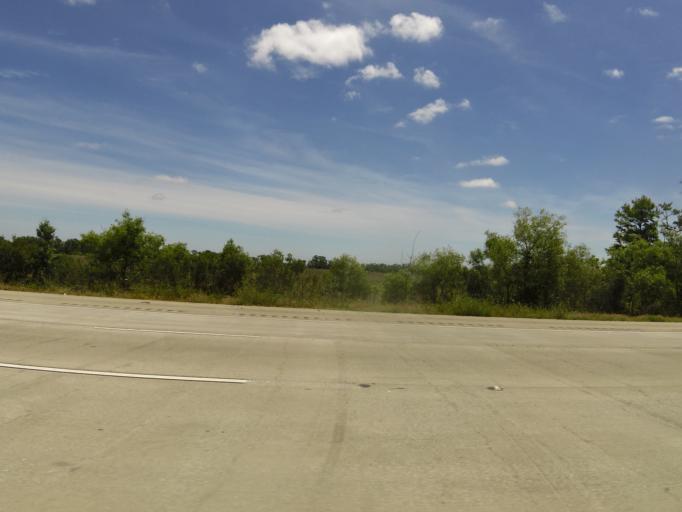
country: US
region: Georgia
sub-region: McIntosh County
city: Darien
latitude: 31.3249
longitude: -81.4725
